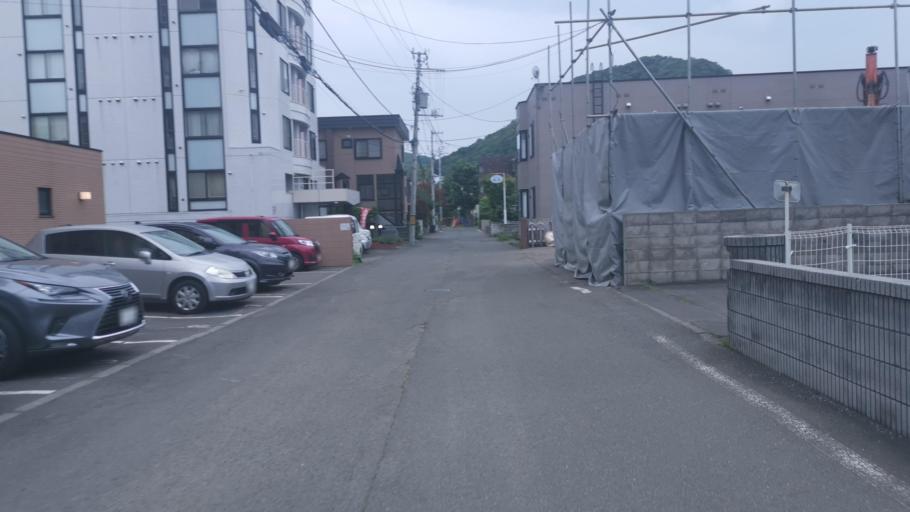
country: JP
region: Hokkaido
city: Sapporo
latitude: 43.0457
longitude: 141.3284
